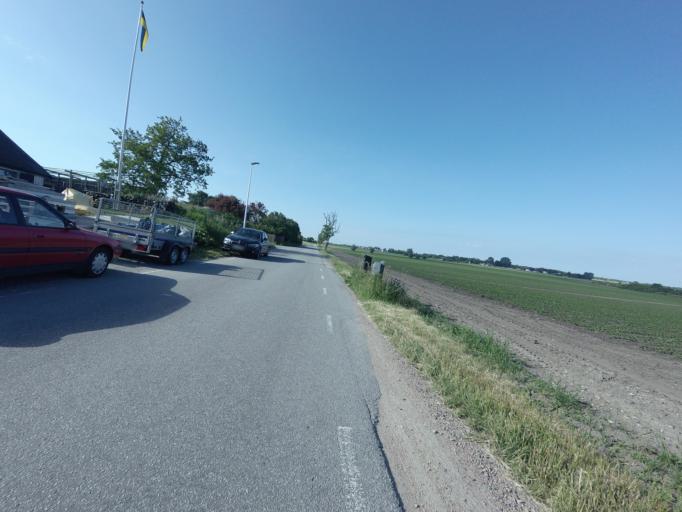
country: SE
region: Skane
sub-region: Trelleborgs Kommun
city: Skare
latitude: 55.4208
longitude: 13.0192
